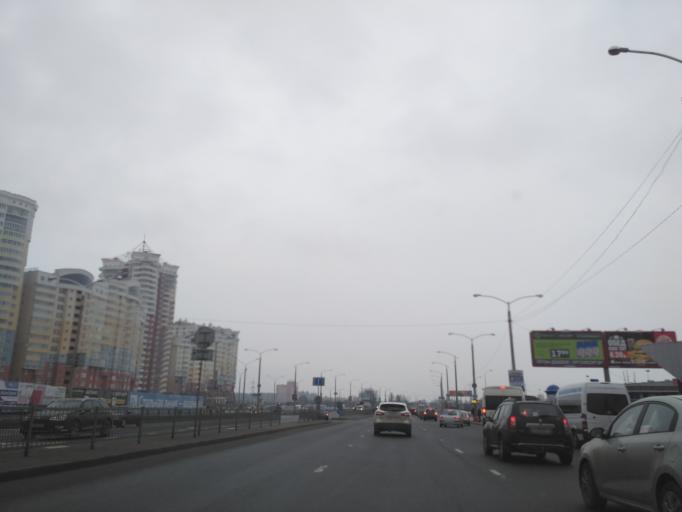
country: BY
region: Minsk
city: Shchomyslitsa
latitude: 53.8488
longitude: 27.4742
